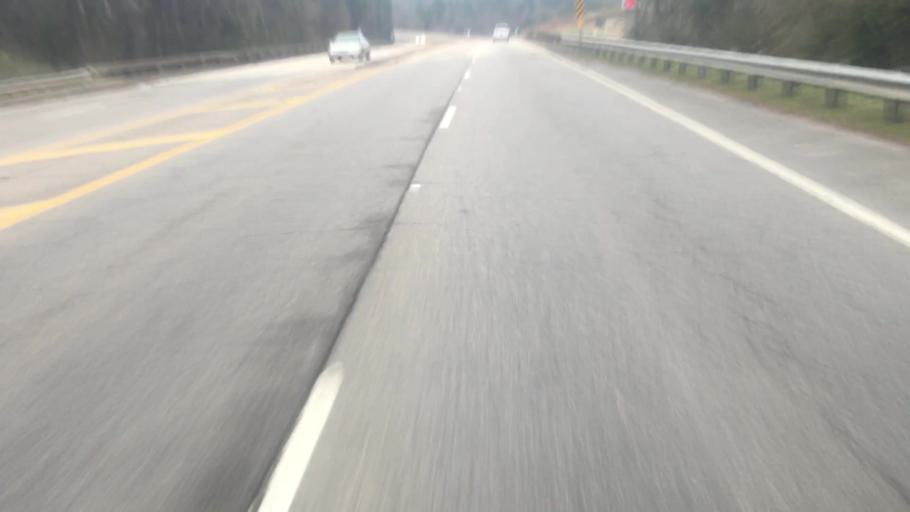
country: US
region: Alabama
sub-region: Walker County
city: Sumiton
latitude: 33.7520
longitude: -87.0597
